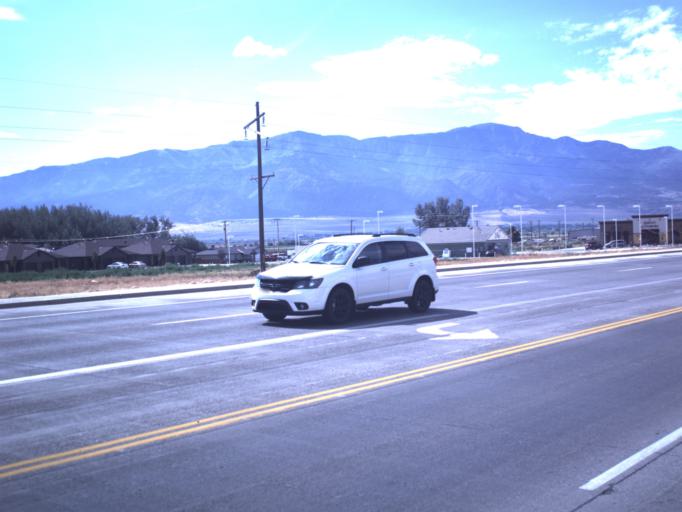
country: US
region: Utah
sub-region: Sevier County
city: Richfield
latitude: 38.7567
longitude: -112.0850
